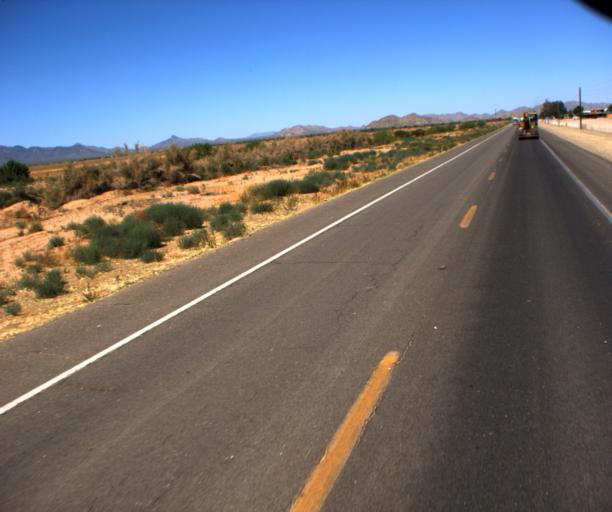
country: US
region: Arizona
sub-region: Pinal County
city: Maricopa
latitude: 32.8794
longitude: -112.0178
